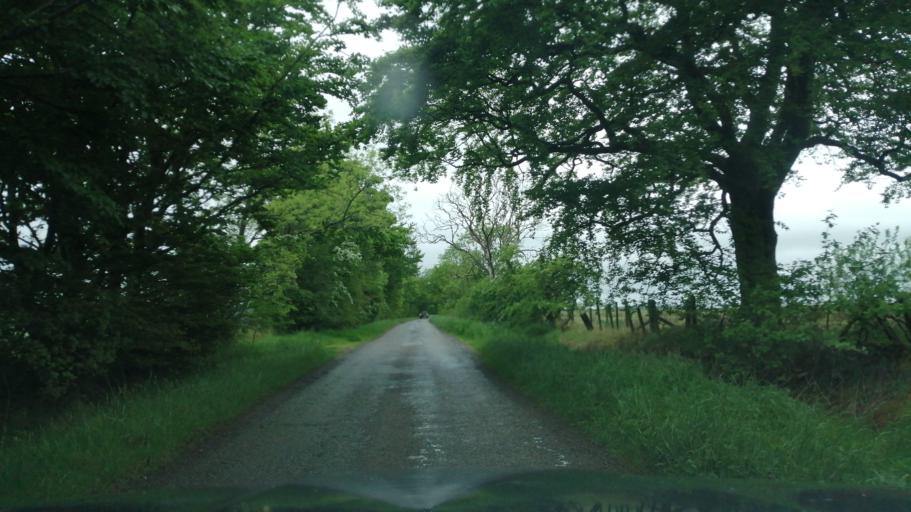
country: GB
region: Scotland
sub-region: Moray
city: Cullen
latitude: 57.5711
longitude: -2.8323
